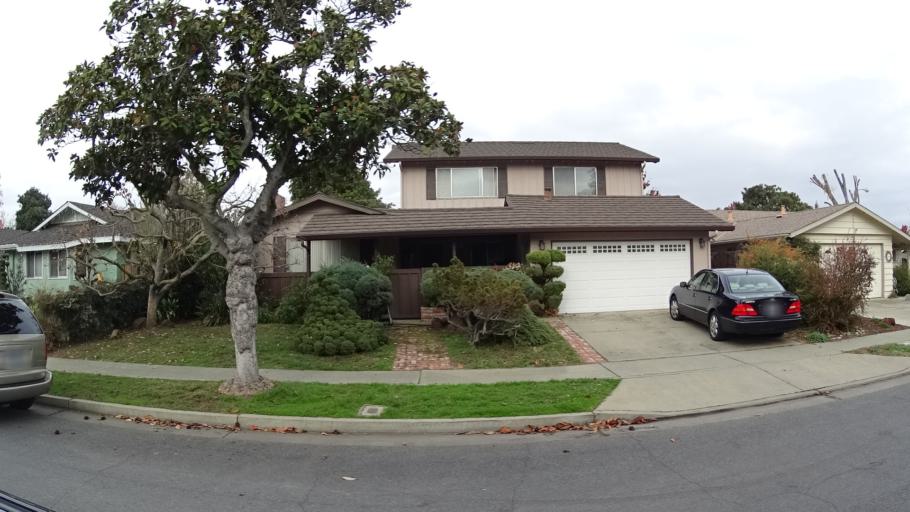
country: US
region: California
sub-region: Santa Clara County
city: Sunnyvale
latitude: 37.3624
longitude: -122.0449
